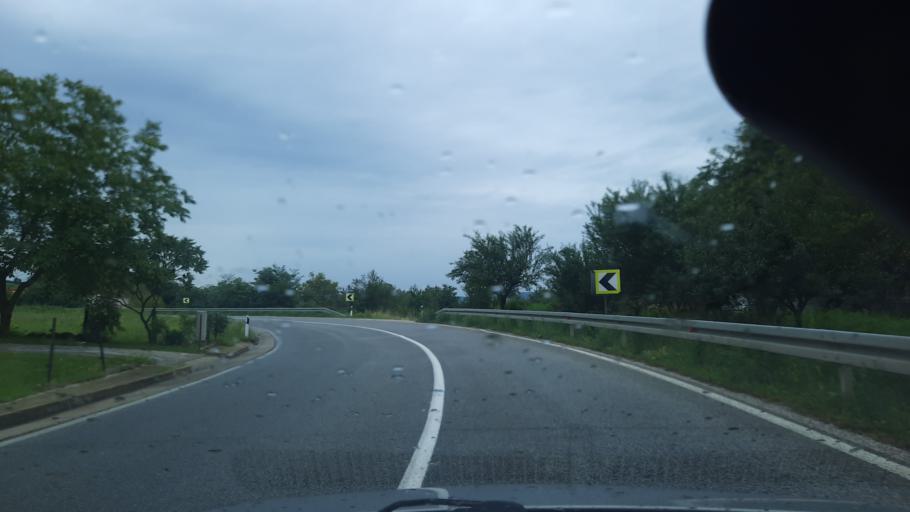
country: RS
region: Central Serbia
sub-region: Sumadijski Okrug
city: Knic
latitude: 43.8924
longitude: 20.7688
